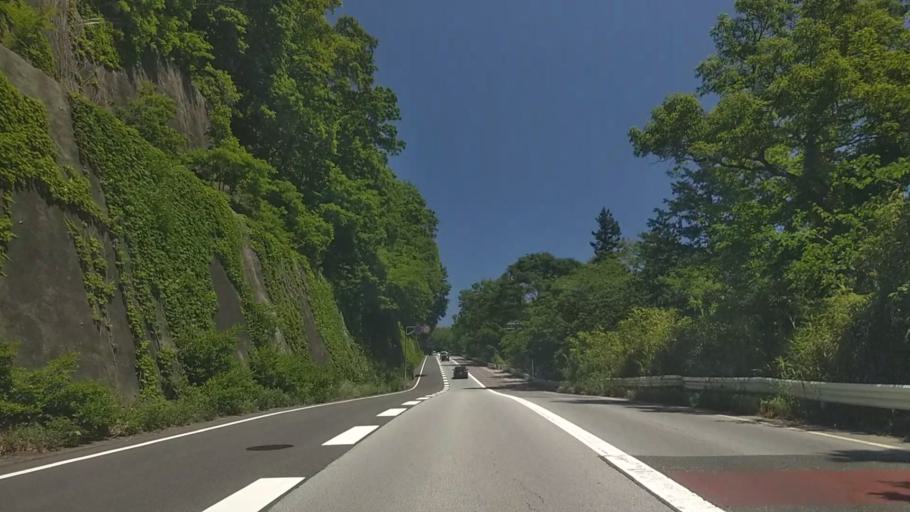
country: JP
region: Yamanashi
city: Nirasaki
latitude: 35.8031
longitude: 138.4264
